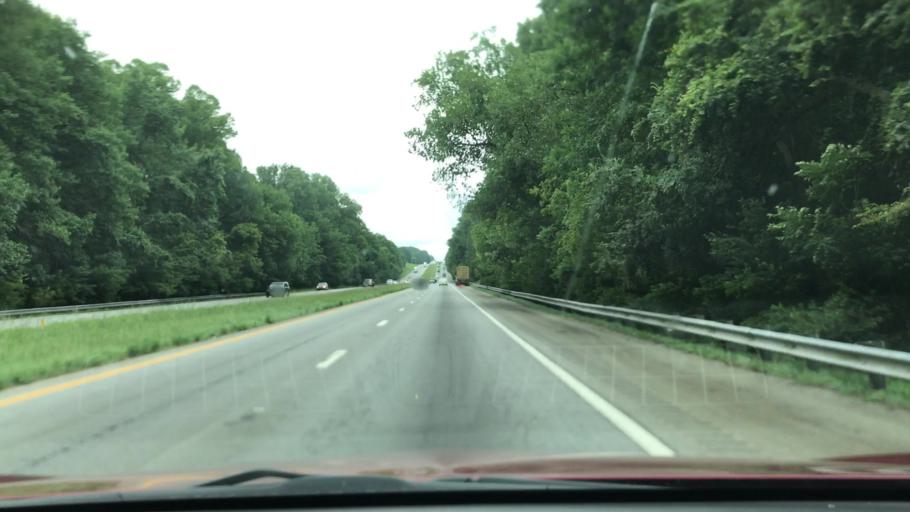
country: US
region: South Carolina
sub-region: Newberry County
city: Newberry
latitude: 34.3566
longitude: -81.6538
